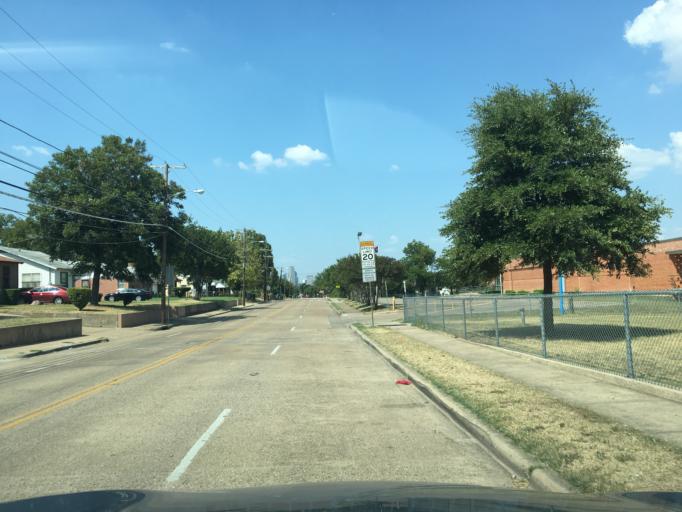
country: US
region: Texas
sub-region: Dallas County
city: Dallas
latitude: 32.7374
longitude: -96.7937
